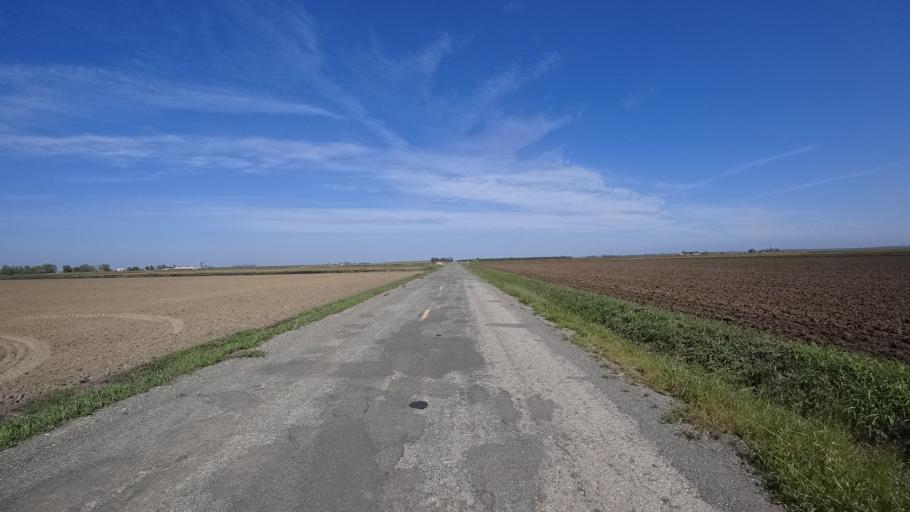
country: US
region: California
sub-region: Glenn County
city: Hamilton City
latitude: 39.5986
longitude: -122.0464
